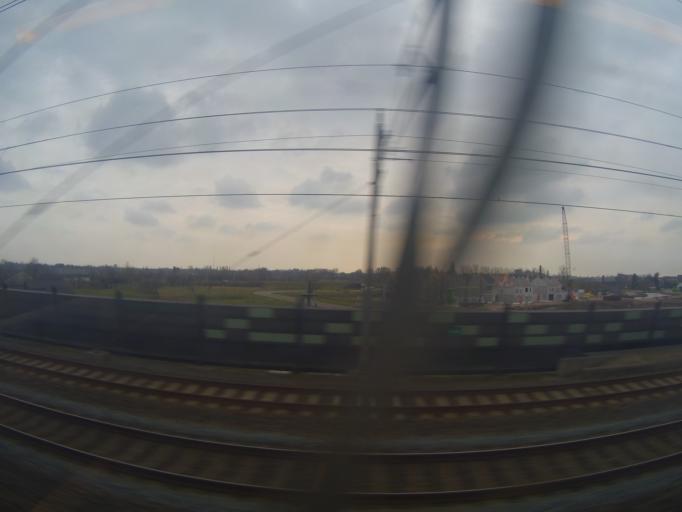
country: NL
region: Utrecht
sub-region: Stichtse Vecht
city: Spechtenkamp
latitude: 52.1020
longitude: 5.0208
